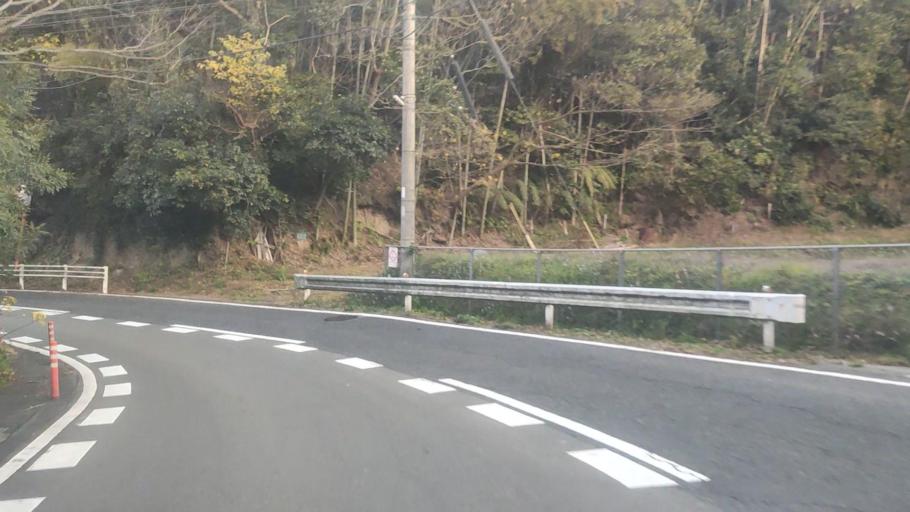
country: JP
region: Kagoshima
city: Kagoshima-shi
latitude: 31.6262
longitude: 130.5538
